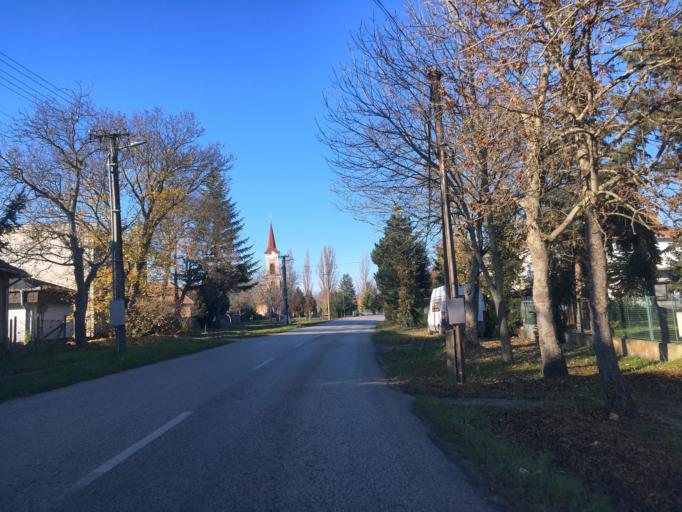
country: SK
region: Nitriansky
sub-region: Okres Komarno
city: Hurbanovo
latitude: 47.9034
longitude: 18.1369
